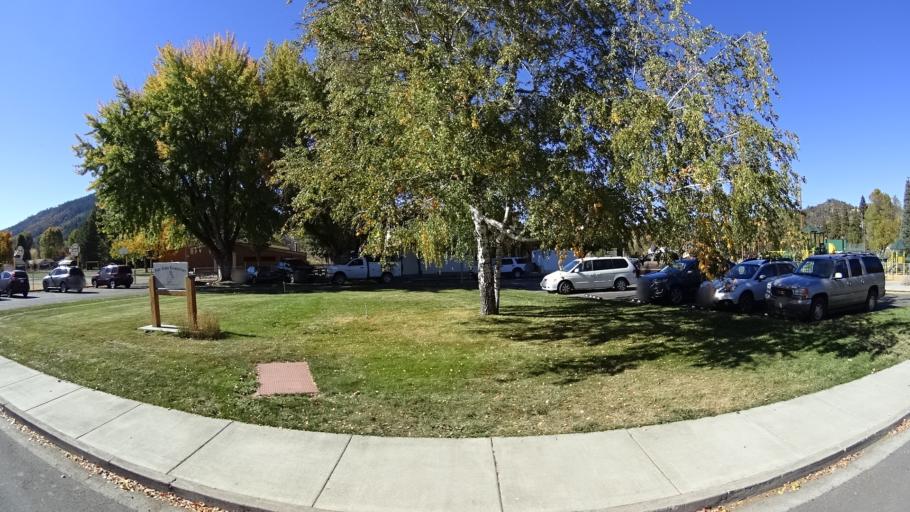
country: US
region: California
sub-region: Siskiyou County
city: Yreka
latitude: 41.6043
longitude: -122.8453
